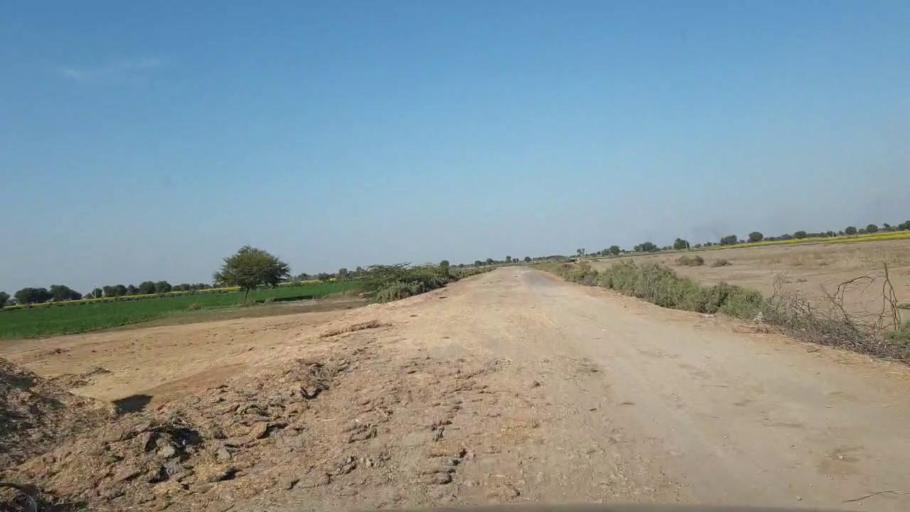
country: PK
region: Sindh
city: Khadro
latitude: 26.1628
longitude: 68.6861
